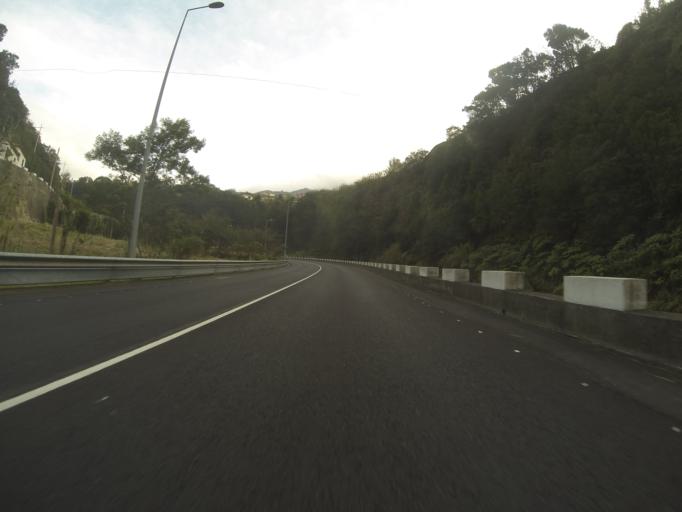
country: PT
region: Madeira
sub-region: Sao Vicente
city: Sao Vicente
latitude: 32.7960
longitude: -17.0402
